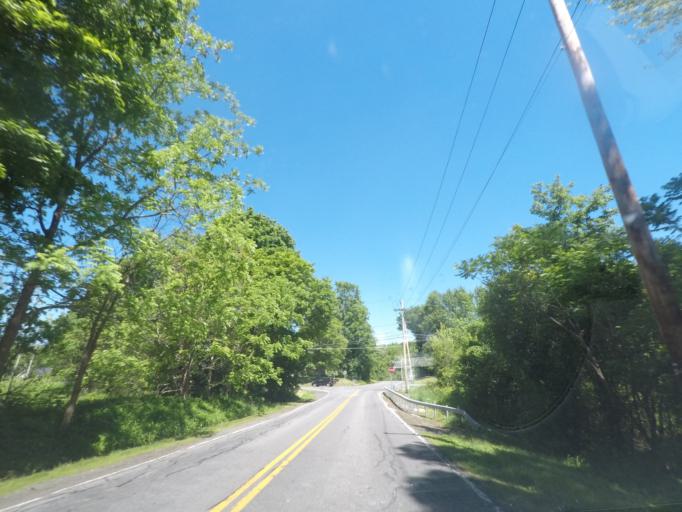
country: US
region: New York
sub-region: Saratoga County
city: Country Knolls
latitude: 42.8681
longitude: -73.8496
